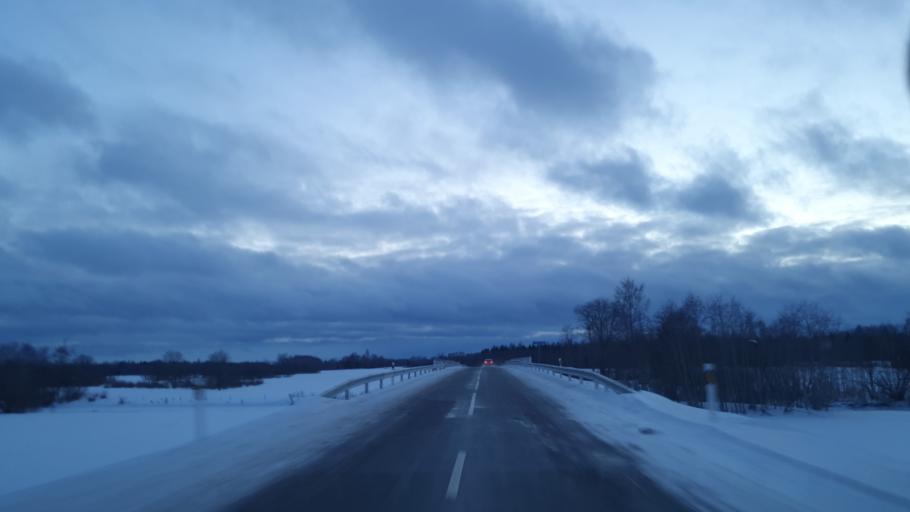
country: EE
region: Jogevamaa
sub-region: Jogeva linn
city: Jogeva
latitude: 58.6022
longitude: 26.3770
